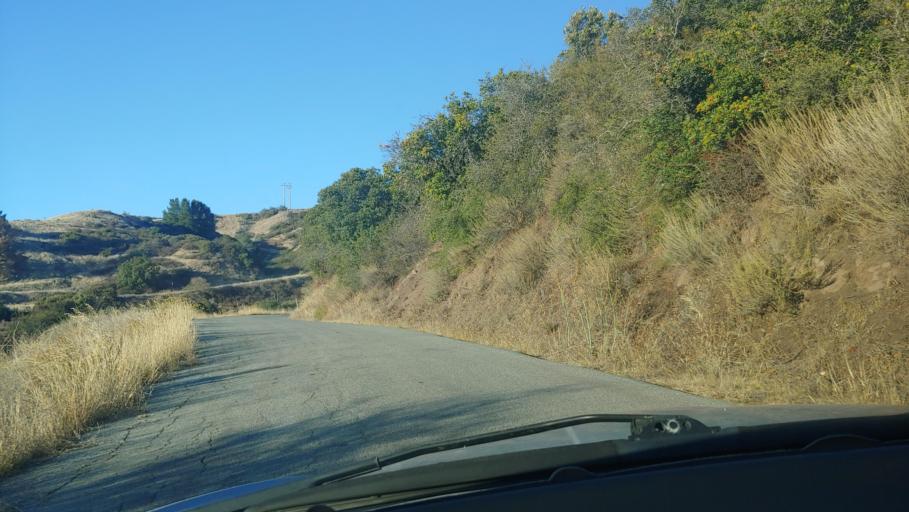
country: US
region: California
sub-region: Santa Barbara County
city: Goleta
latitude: 34.5138
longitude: -119.7964
